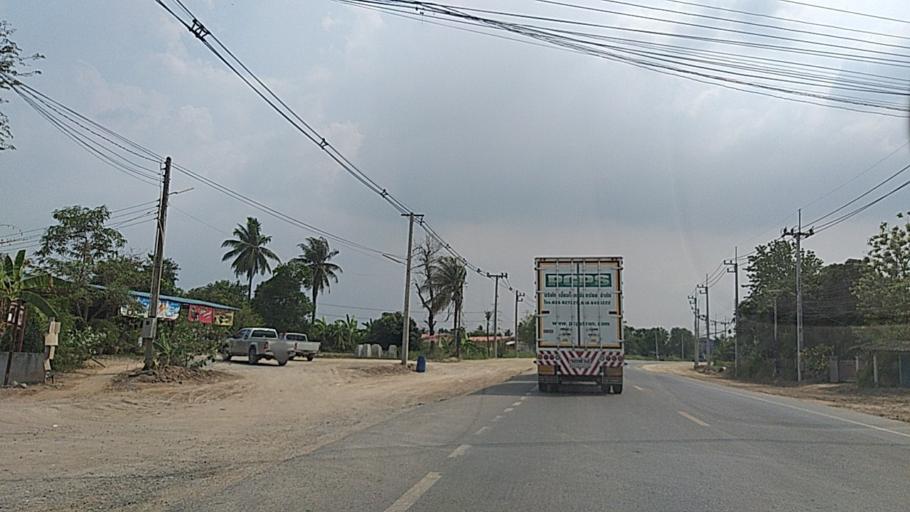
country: TH
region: Chon Buri
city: Ban Bueng
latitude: 13.3496
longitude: 101.1953
